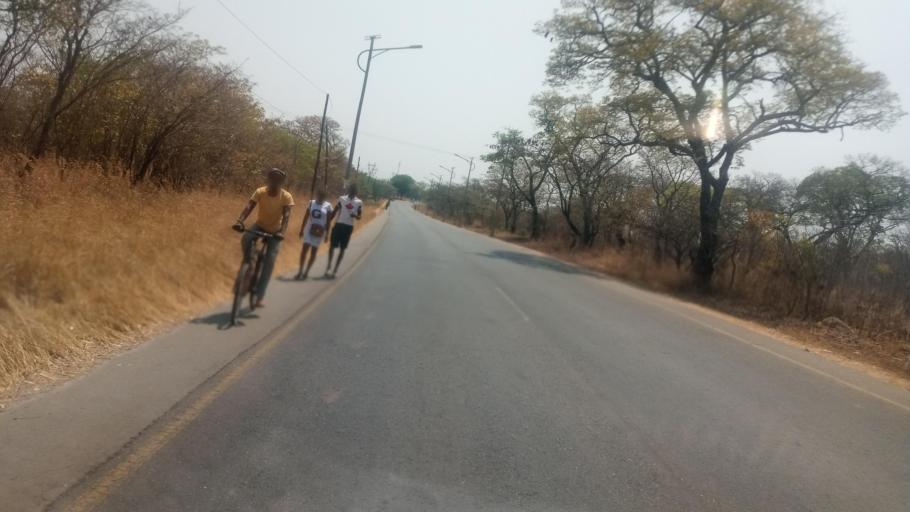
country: ZM
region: Lusaka
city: Lusaka
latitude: -15.4714
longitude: 28.4264
